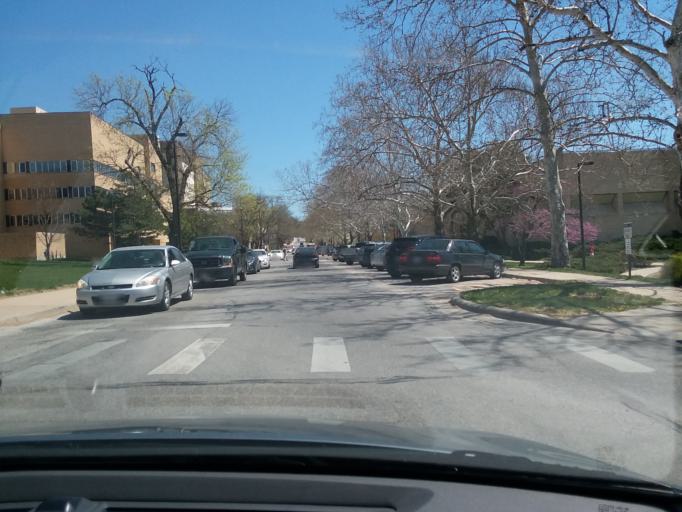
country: US
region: Kansas
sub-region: Douglas County
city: Lawrence
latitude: 38.9553
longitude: -95.2511
